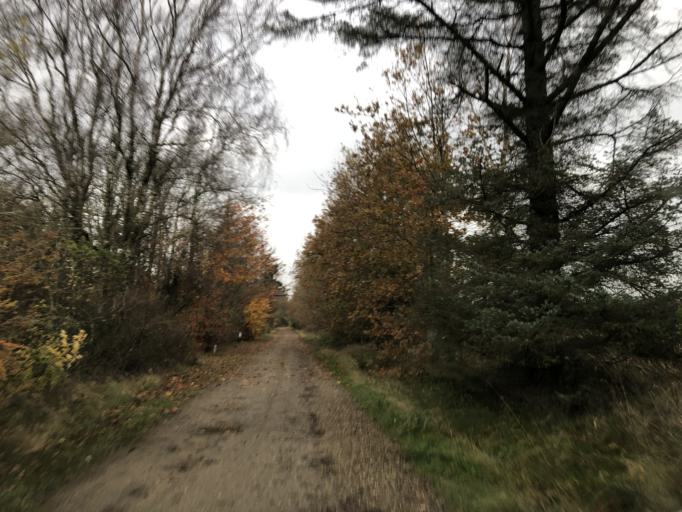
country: DK
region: Central Jutland
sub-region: Holstebro Kommune
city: Ulfborg
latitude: 56.3165
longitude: 8.2170
